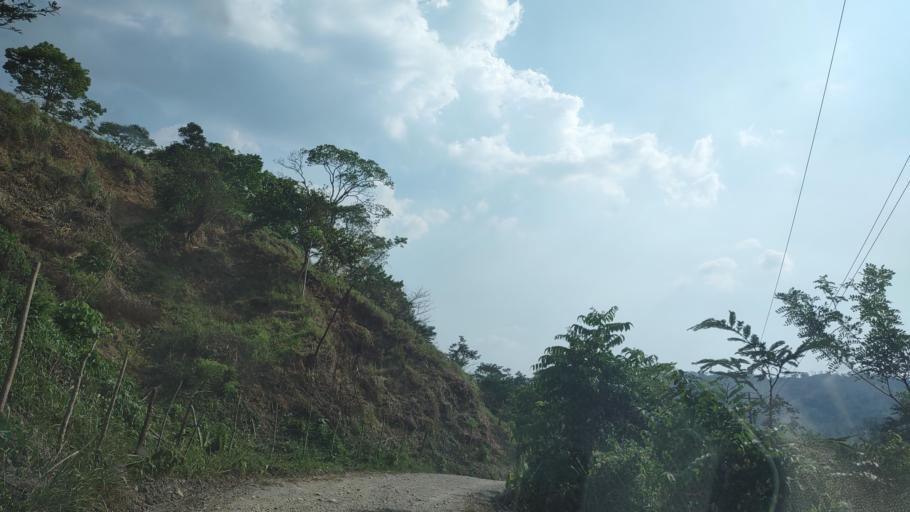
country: MX
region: Chiapas
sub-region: Tecpatan
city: Raudales Malpaso
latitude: 17.3171
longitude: -93.7420
